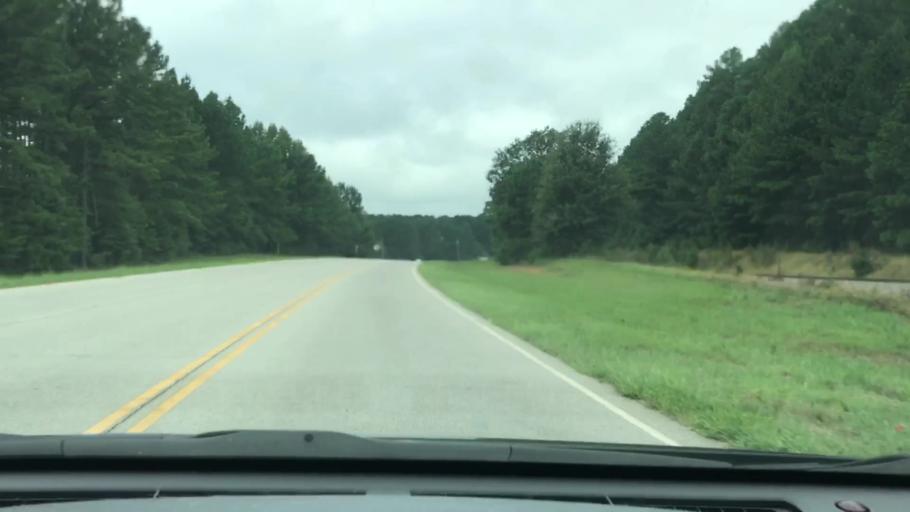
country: US
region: Georgia
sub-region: Warren County
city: Firing Range
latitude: 33.4836
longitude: -82.7889
